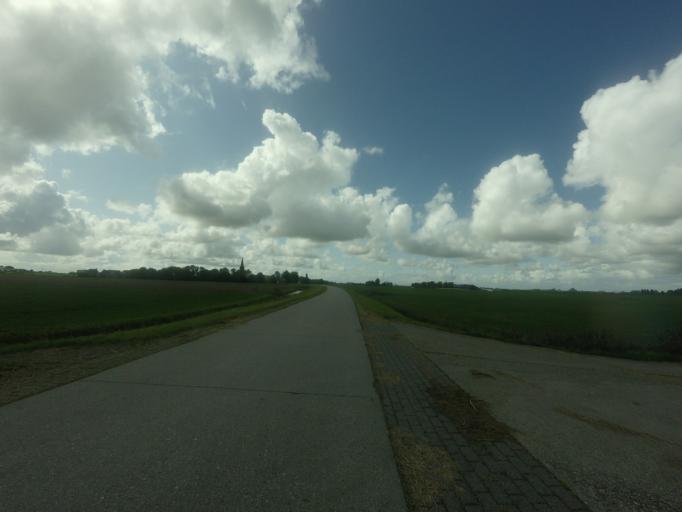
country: NL
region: Friesland
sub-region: Sudwest Fryslan
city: Scharnegoutum
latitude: 53.0780
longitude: 5.6429
